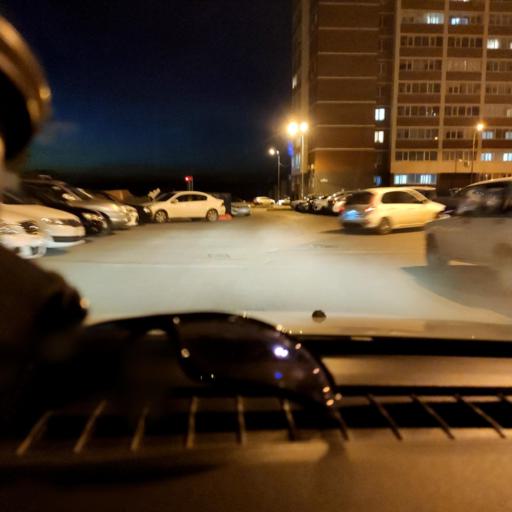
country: RU
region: Samara
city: Samara
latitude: 53.2420
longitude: 50.1793
